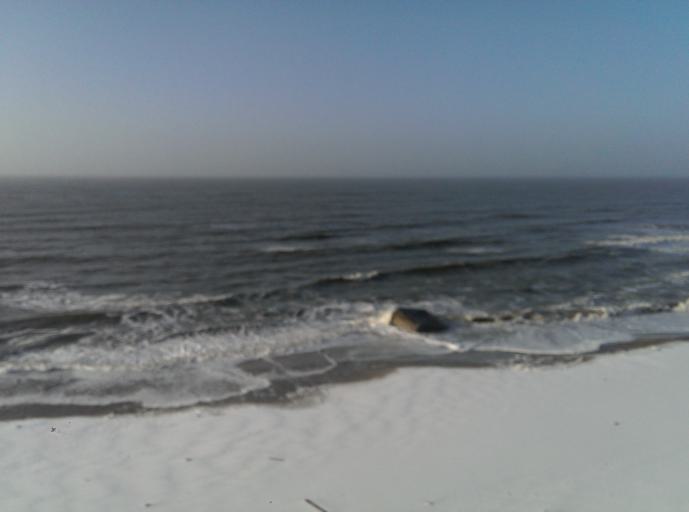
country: DK
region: Central Jutland
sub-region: Holstebro Kommune
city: Ulfborg
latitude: 56.2720
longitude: 8.1293
